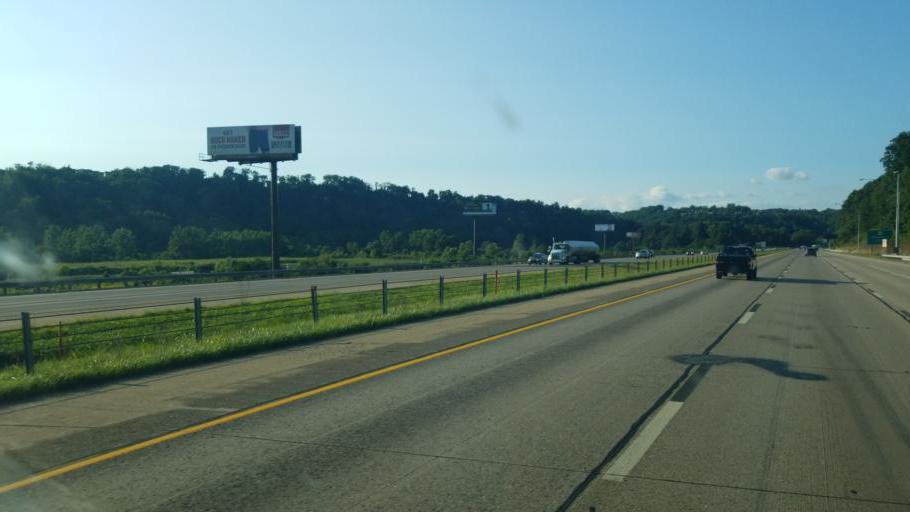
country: US
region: Pennsylvania
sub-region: Allegheny County
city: Bridgeville
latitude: 40.3618
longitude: -80.1187
